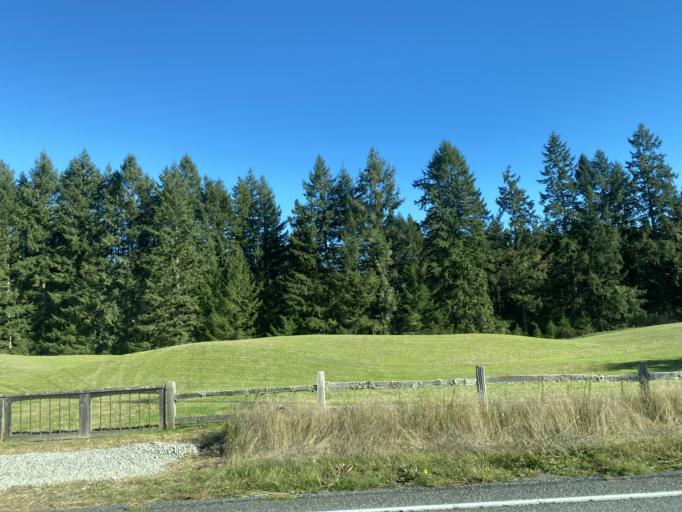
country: US
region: Washington
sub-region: Island County
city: Langley
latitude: 48.0089
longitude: -122.4260
